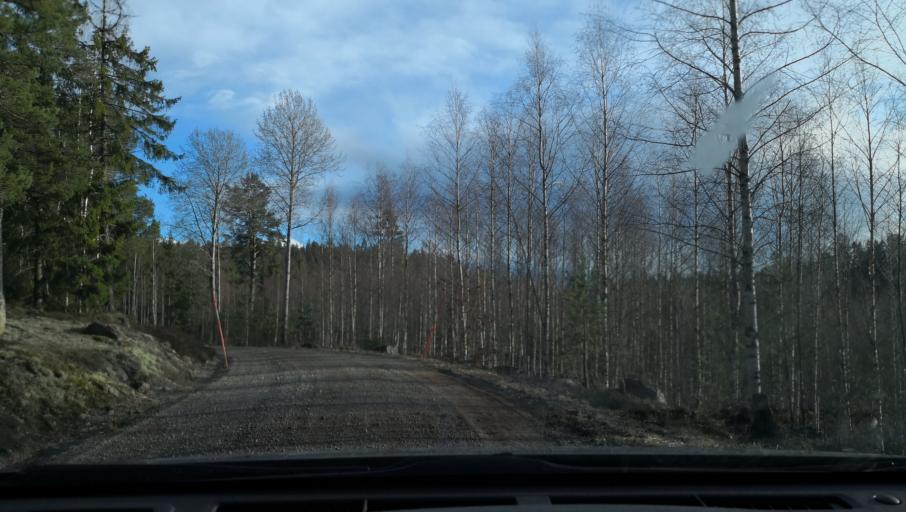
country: SE
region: Vaestmanland
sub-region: Arboga Kommun
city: Arboga
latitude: 59.4388
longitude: 15.7524
